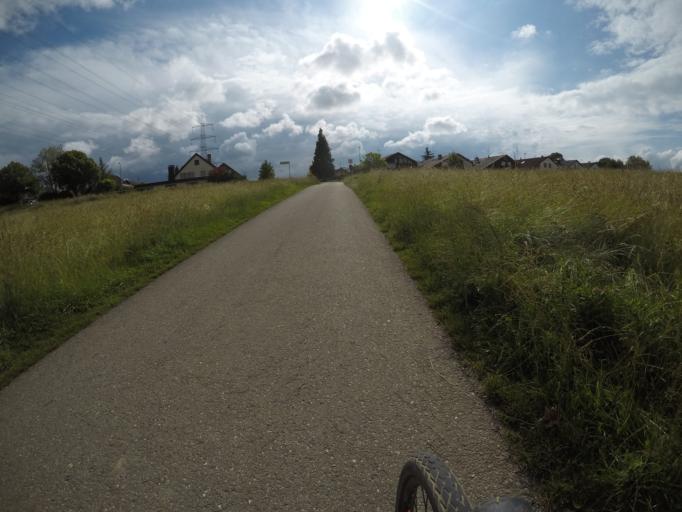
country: DE
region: Baden-Wuerttemberg
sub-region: Regierungsbezirk Stuttgart
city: Frickenhausen
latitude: 48.6135
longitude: 9.3588
